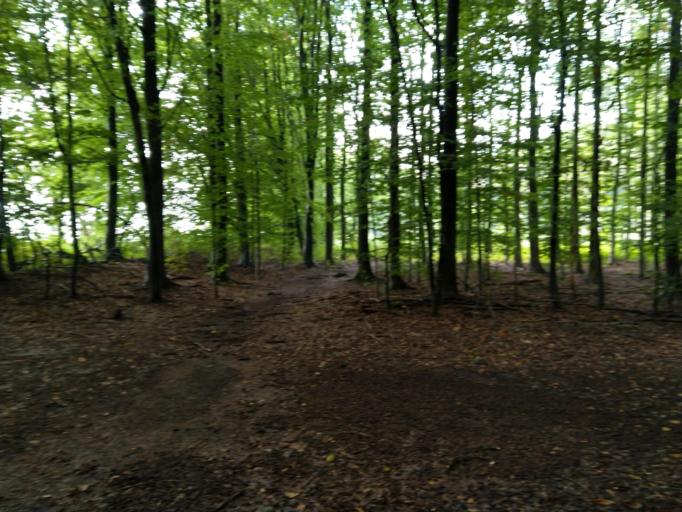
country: DE
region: North Rhine-Westphalia
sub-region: Regierungsbezirk Detmold
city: Bad Salzuflen
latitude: 52.0846
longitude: 8.7783
